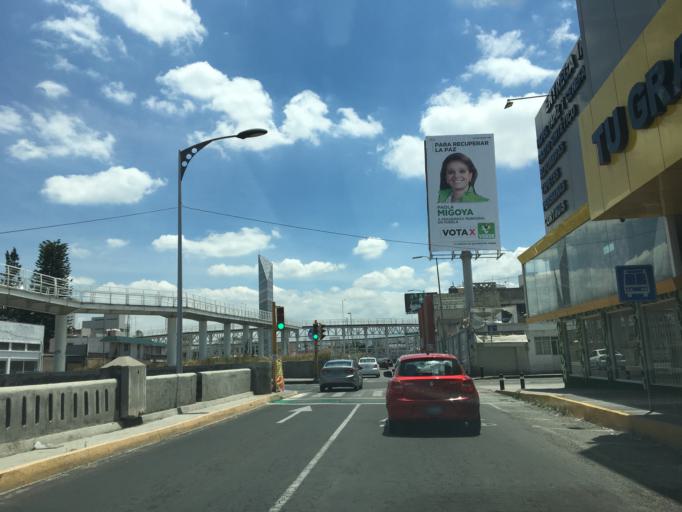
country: MX
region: Puebla
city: Puebla
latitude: 19.0570
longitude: -98.2202
